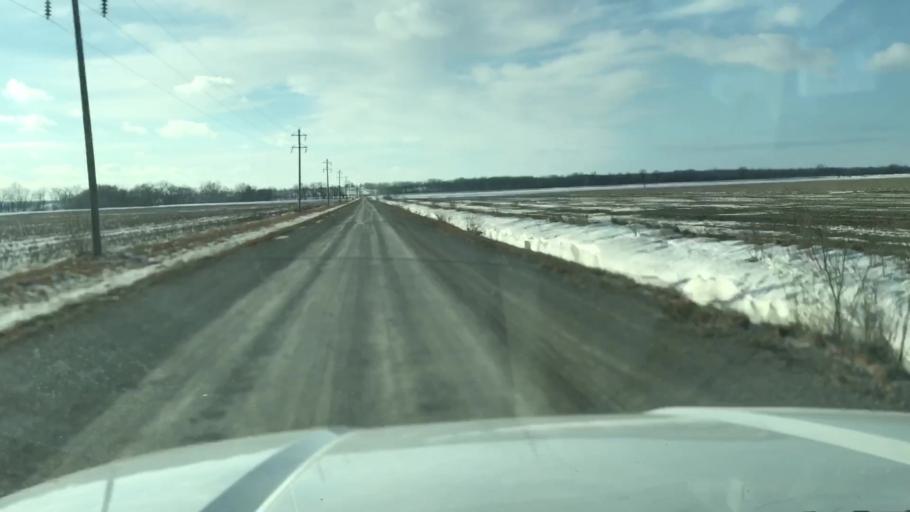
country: US
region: Missouri
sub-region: Holt County
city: Oregon
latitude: 40.1300
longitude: -95.0304
